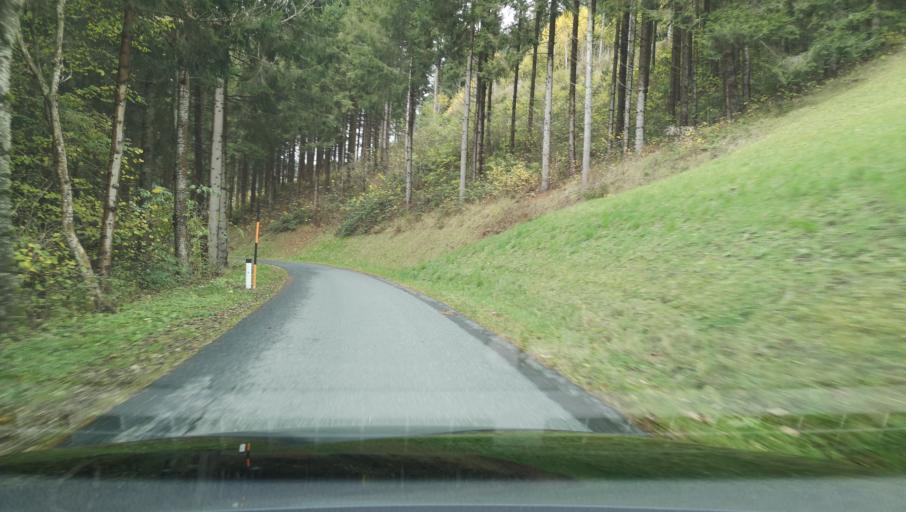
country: AT
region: Styria
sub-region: Politischer Bezirk Weiz
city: Birkfeld
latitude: 47.3696
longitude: 15.6303
